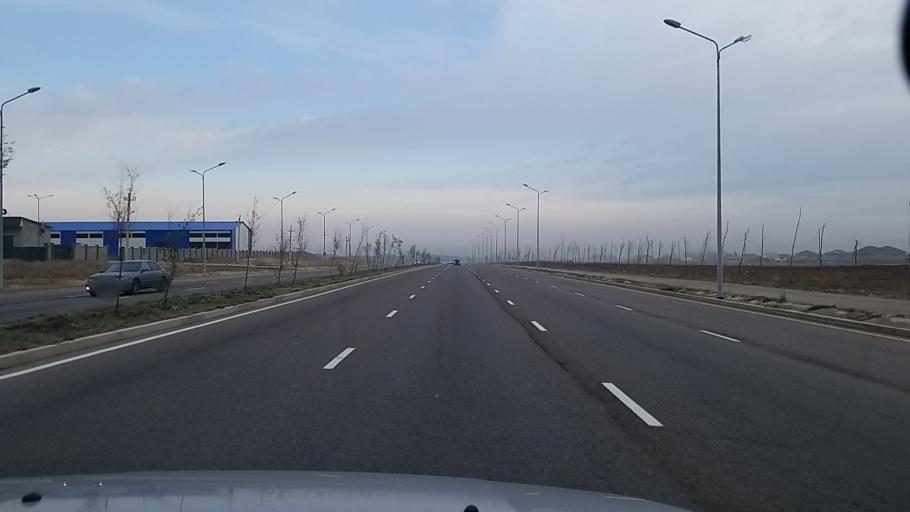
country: KZ
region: Almaty Oblysy
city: Burunday
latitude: 43.3385
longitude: 76.8336
